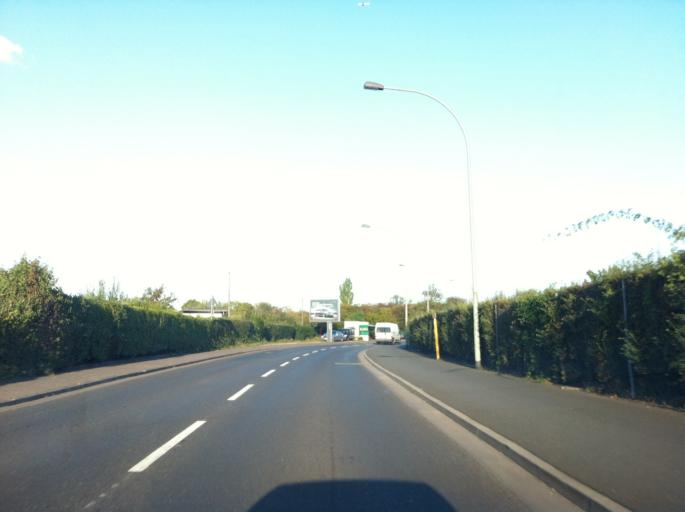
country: DE
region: Hesse
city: Niederrad
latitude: 50.1125
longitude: 8.6043
